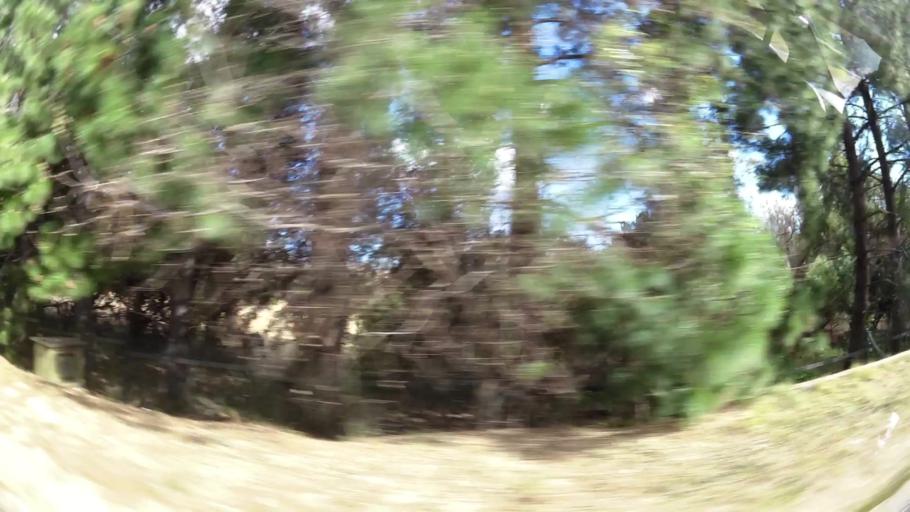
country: ZA
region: Gauteng
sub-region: West Rand District Municipality
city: Muldersdriseloop
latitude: -26.0879
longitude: 27.8534
